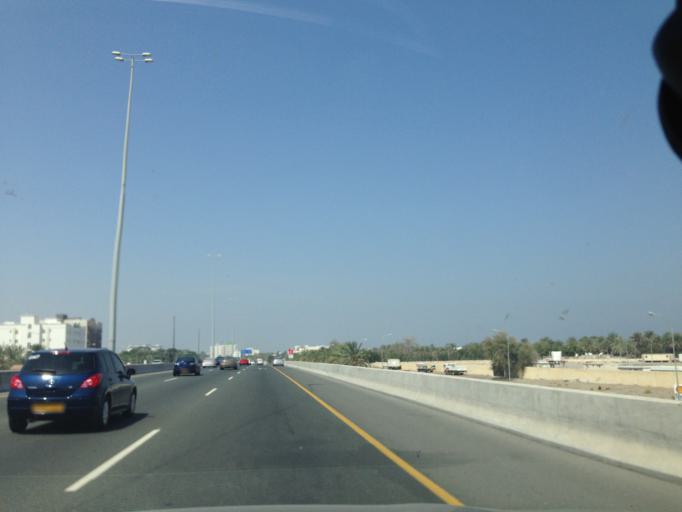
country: OM
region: Muhafazat Masqat
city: As Sib al Jadidah
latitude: 23.6422
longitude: 58.2234
